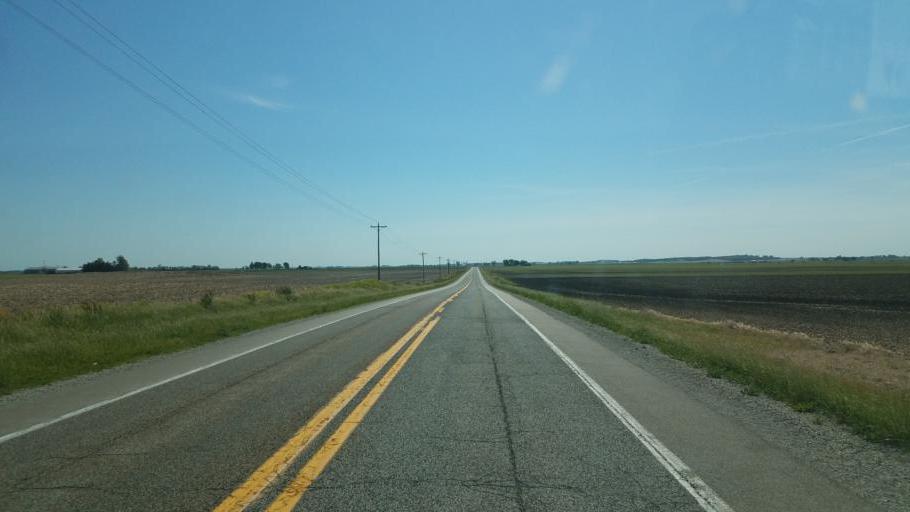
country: US
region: Illinois
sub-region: Mason County
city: Mason City
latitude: 40.3040
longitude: -89.7525
